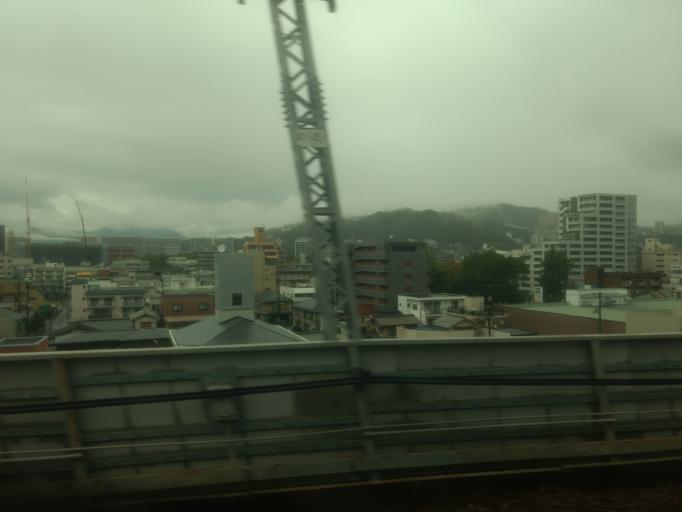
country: JP
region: Hiroshima
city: Hiroshima-shi
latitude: 34.4078
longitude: 132.4629
